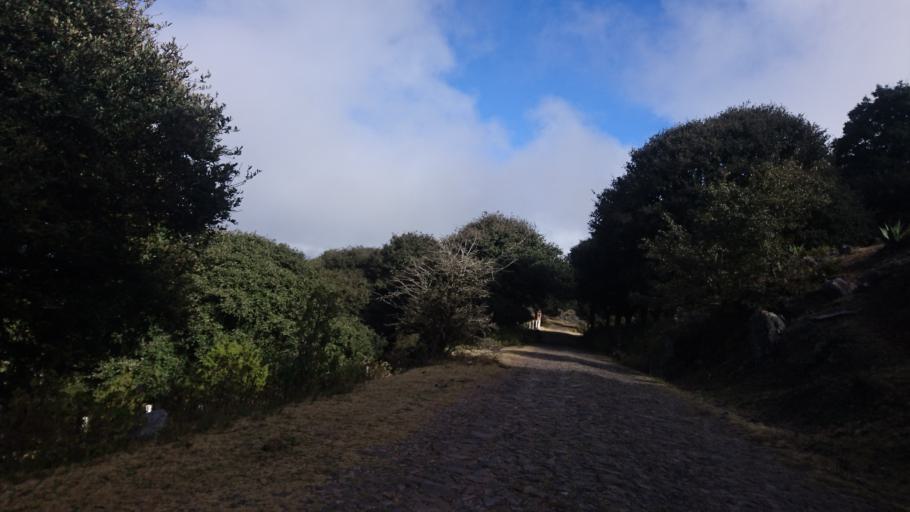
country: MX
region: San Luis Potosi
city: Zaragoza
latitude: 22.0681
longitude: -100.6466
